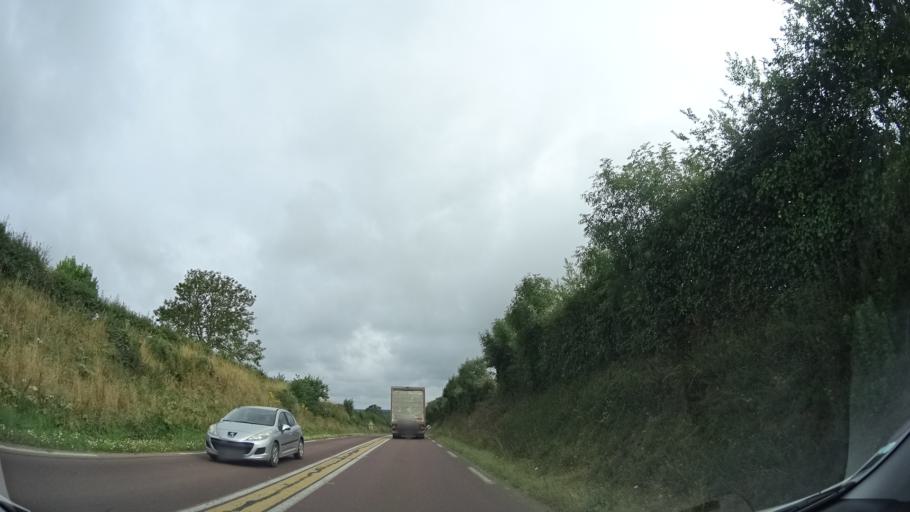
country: FR
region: Lower Normandy
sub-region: Departement de la Manche
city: Gouville-sur-Mer
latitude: 49.1330
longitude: -1.5027
